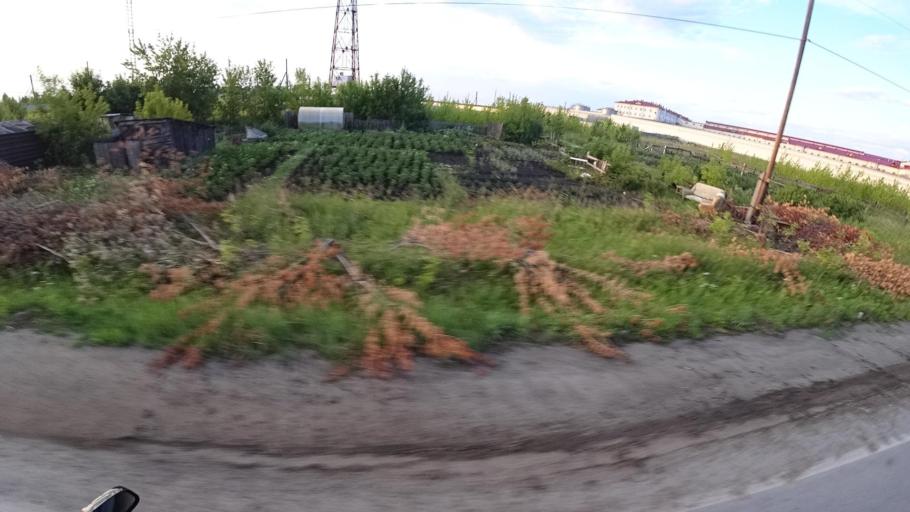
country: RU
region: Sverdlovsk
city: Kamyshlov
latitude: 56.8567
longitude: 62.7327
